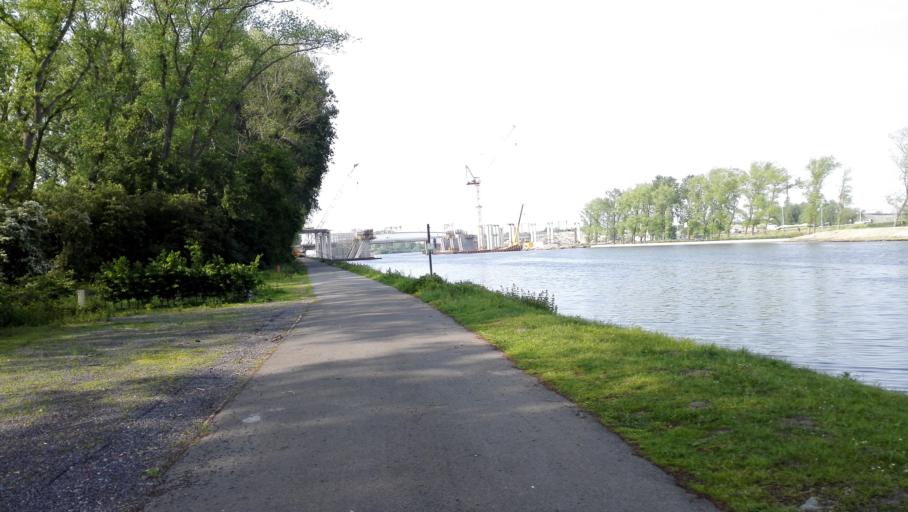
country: BE
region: Flanders
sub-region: Provincie West-Vlaanderen
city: Zuienkerke
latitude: 51.2701
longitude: 3.2122
